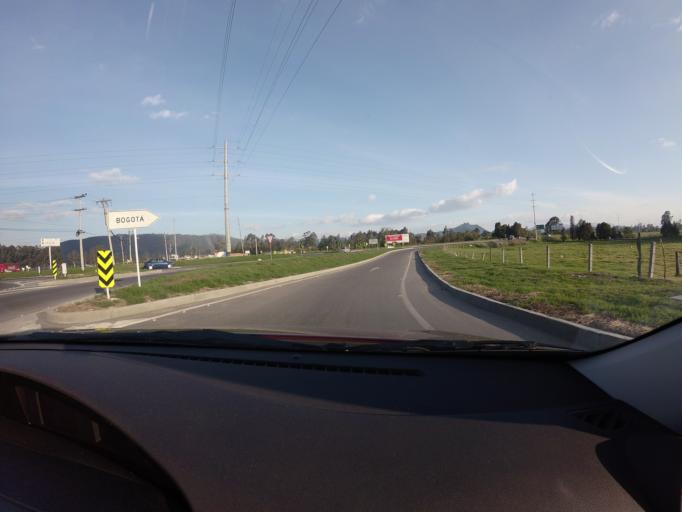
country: CO
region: Cundinamarca
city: Zipaquira
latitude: 5.0094
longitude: -73.9887
